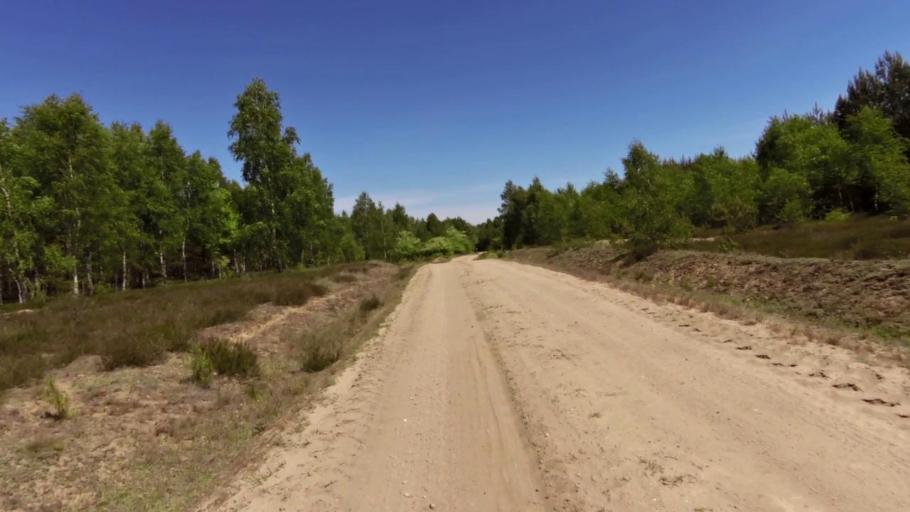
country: PL
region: West Pomeranian Voivodeship
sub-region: Powiat szczecinecki
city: Borne Sulinowo
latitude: 53.5848
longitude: 16.6516
